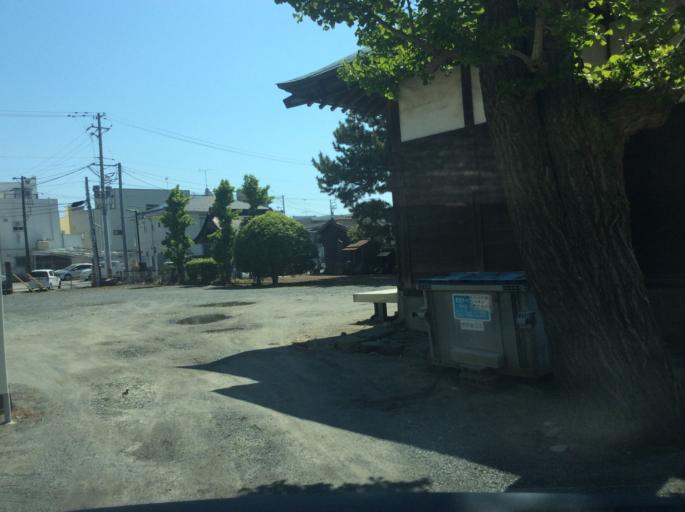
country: JP
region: Fukushima
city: Iwaki
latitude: 36.9511
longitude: 140.9036
